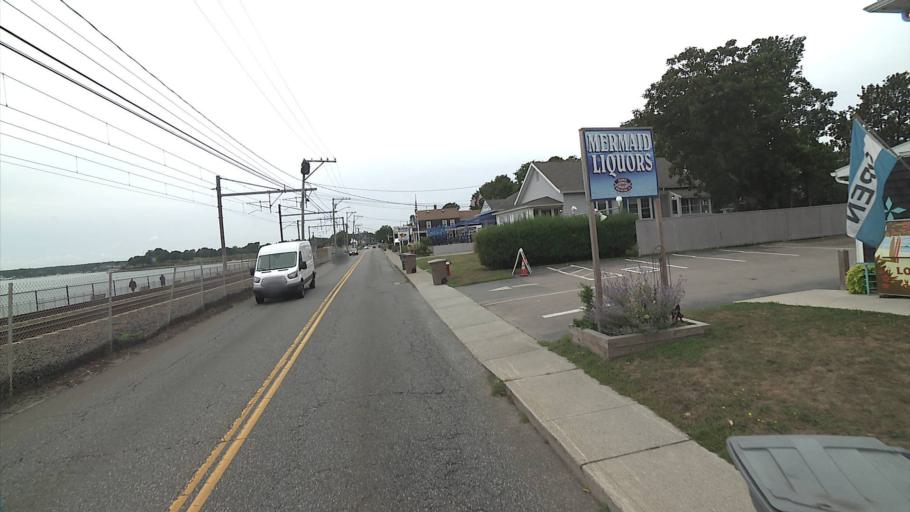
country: US
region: Connecticut
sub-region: New London County
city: Niantic
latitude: 41.3243
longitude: -72.1882
